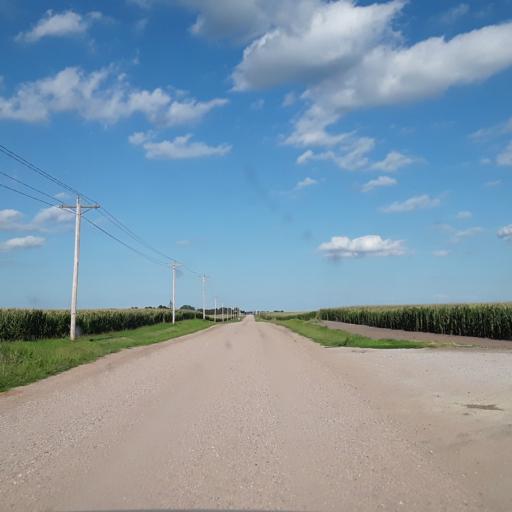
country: US
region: Nebraska
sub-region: Hall County
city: Wood River
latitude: 40.9168
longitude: -98.5987
